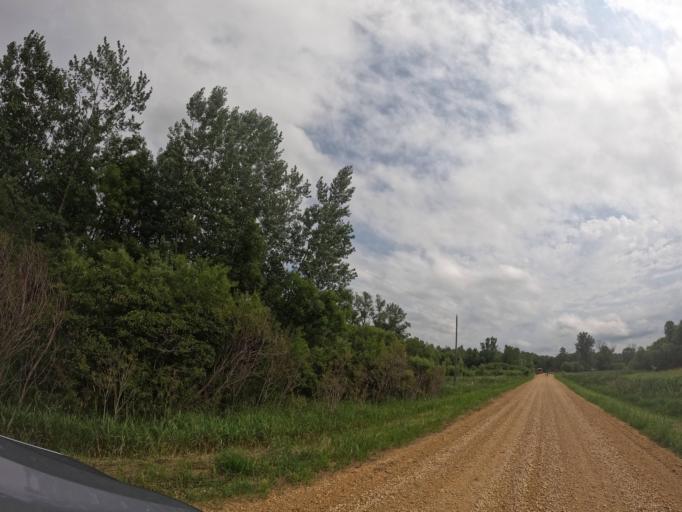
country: US
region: Iowa
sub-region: Clinton County
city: De Witt
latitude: 41.7741
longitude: -90.5828
